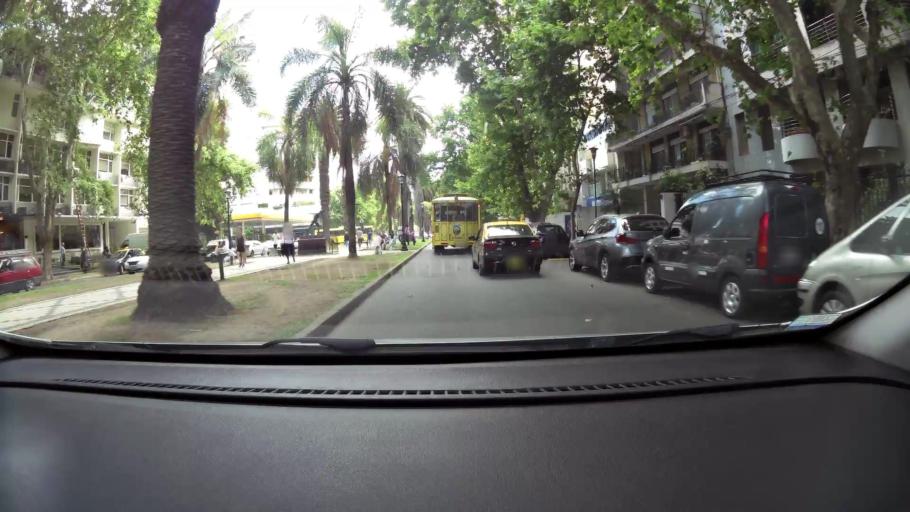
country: AR
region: Santa Fe
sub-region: Departamento de Rosario
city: Rosario
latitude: -32.9445
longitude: -60.6534
